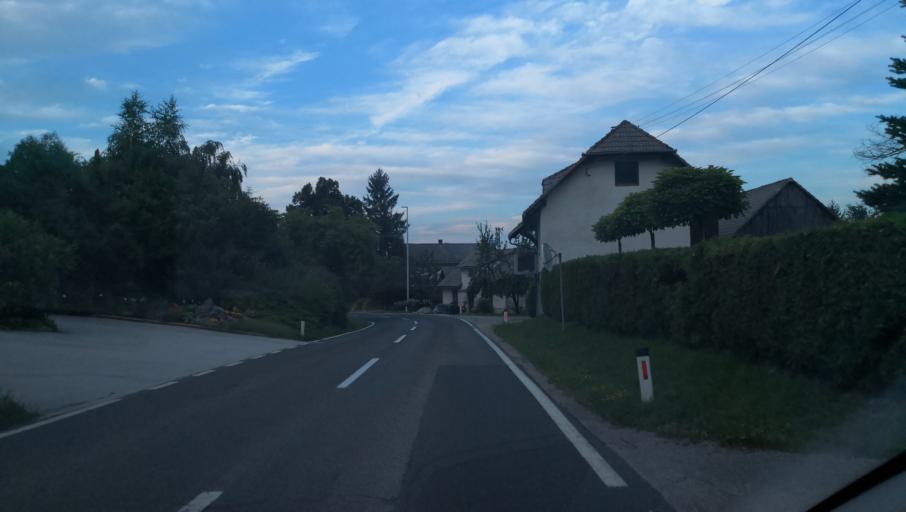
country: SI
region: Metlika
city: Metlika
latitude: 45.6936
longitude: 15.2592
